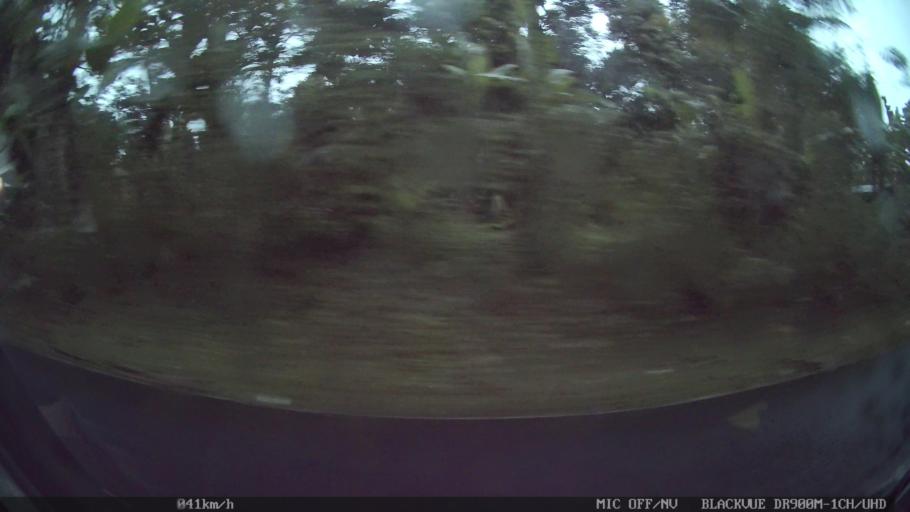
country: ID
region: Bali
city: Banjar Taro Kelod
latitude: -8.3607
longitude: 115.2723
